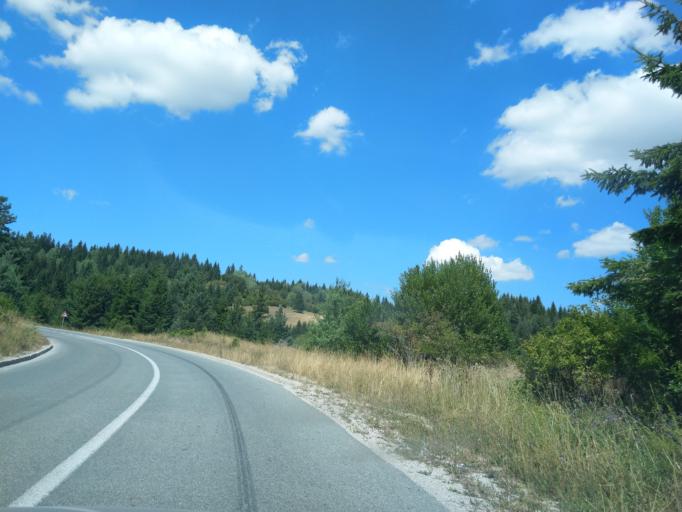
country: RS
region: Central Serbia
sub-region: Zlatiborski Okrug
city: Nova Varos
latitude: 43.3916
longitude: 19.8478
